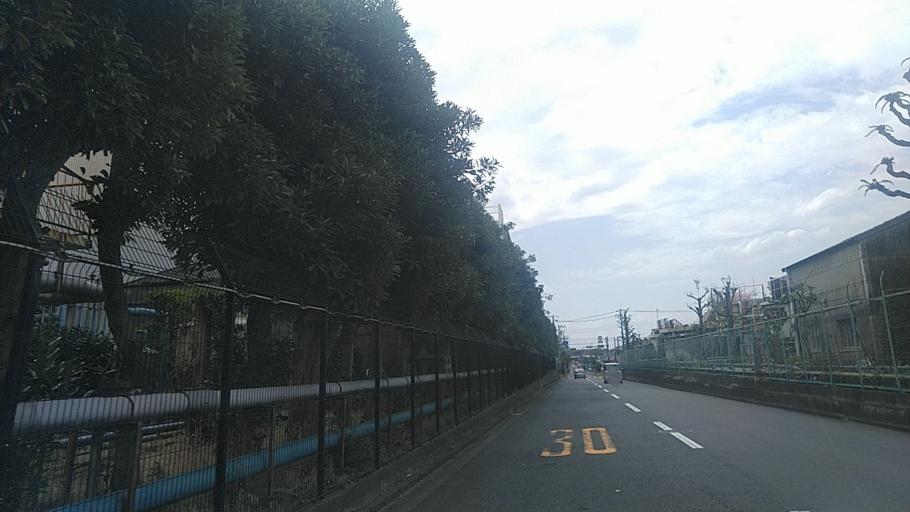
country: JP
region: Kanagawa
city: Fujisawa
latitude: 35.3841
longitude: 139.4462
